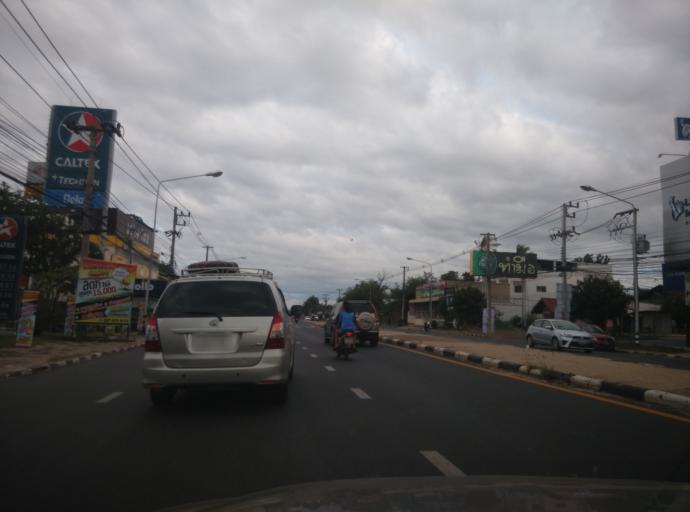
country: TH
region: Sisaket
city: Si Sa Ket
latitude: 15.1108
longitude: 104.3540
